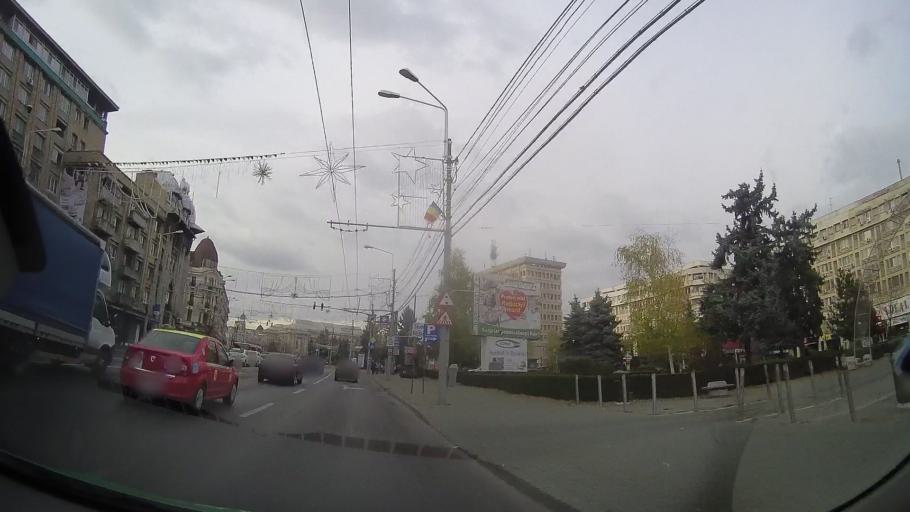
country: RO
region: Prahova
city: Ploiesti
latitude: 44.9398
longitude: 26.0245
